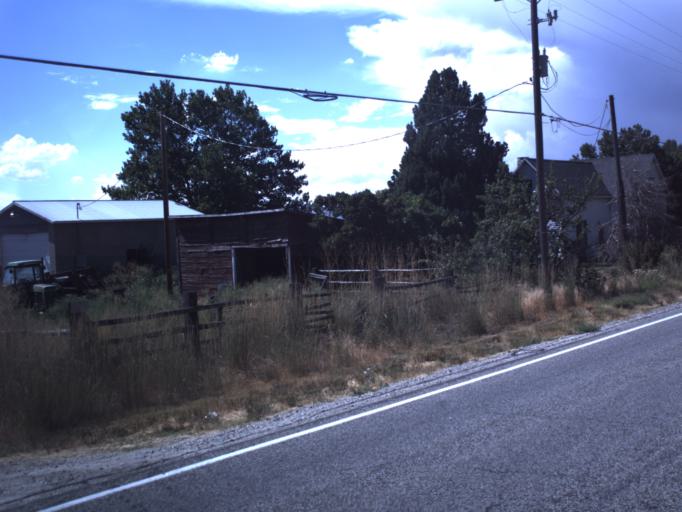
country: US
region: Utah
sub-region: Box Elder County
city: Honeyville
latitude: 41.6101
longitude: -112.0618
